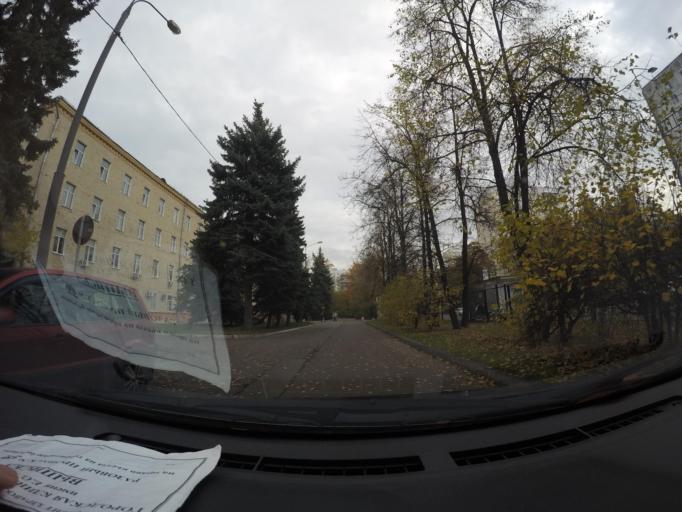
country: RU
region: Moskovskaya
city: Novogireyevo
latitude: 55.7555
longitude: 37.8129
